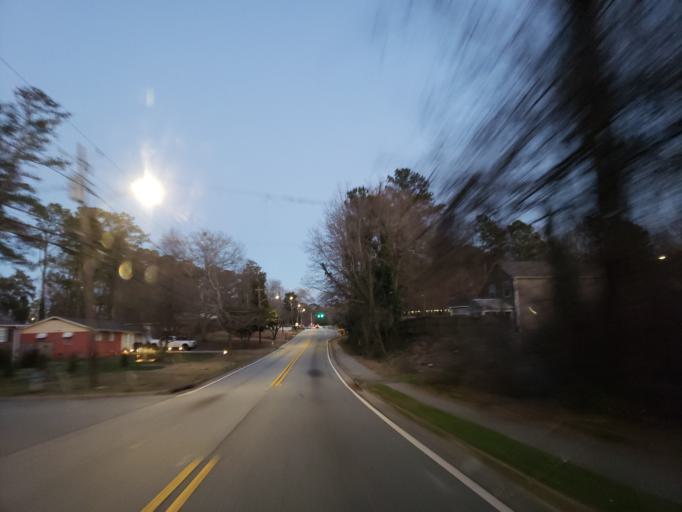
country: US
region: Georgia
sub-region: Cobb County
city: Smyrna
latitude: 33.8675
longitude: -84.5424
